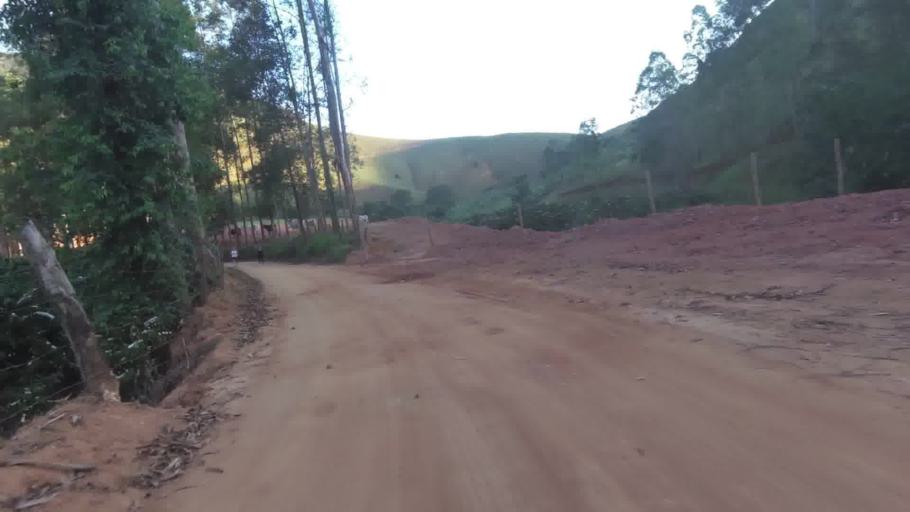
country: BR
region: Espirito Santo
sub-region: Alfredo Chaves
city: Alfredo Chaves
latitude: -20.6110
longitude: -40.7190
